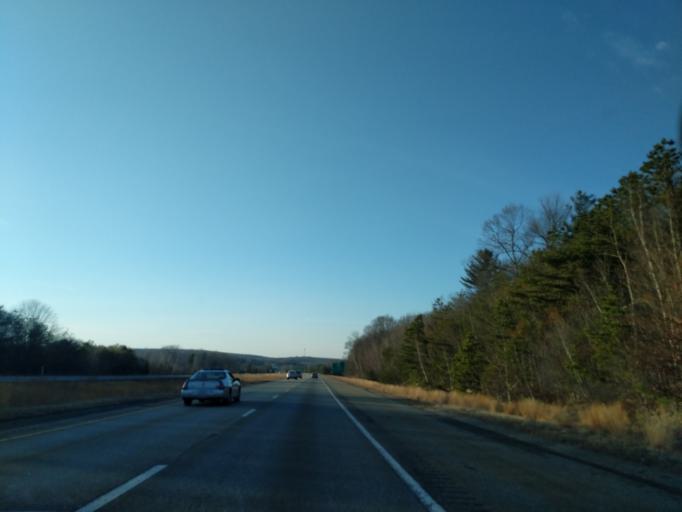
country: US
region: Massachusetts
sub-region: Worcester County
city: Millville
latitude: 42.0192
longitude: -71.5968
